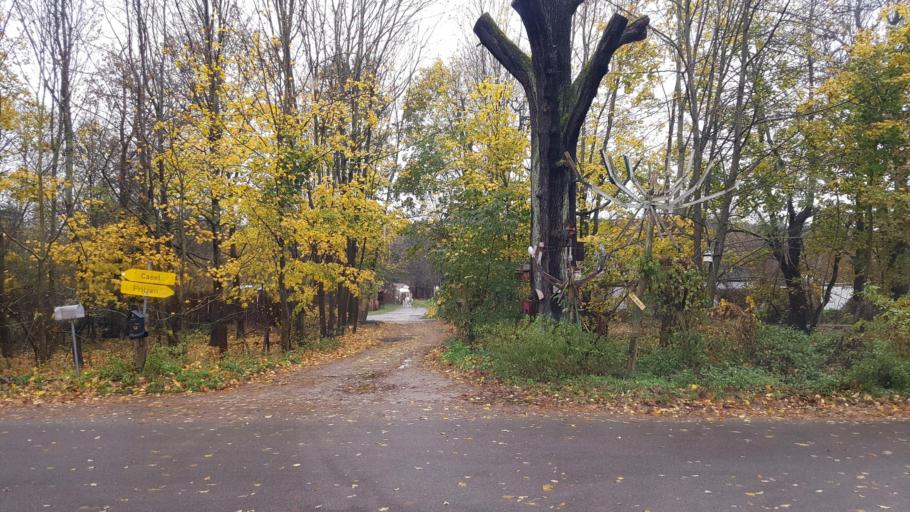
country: DE
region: Brandenburg
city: Altdobern
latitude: 51.6696
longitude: 14.1097
